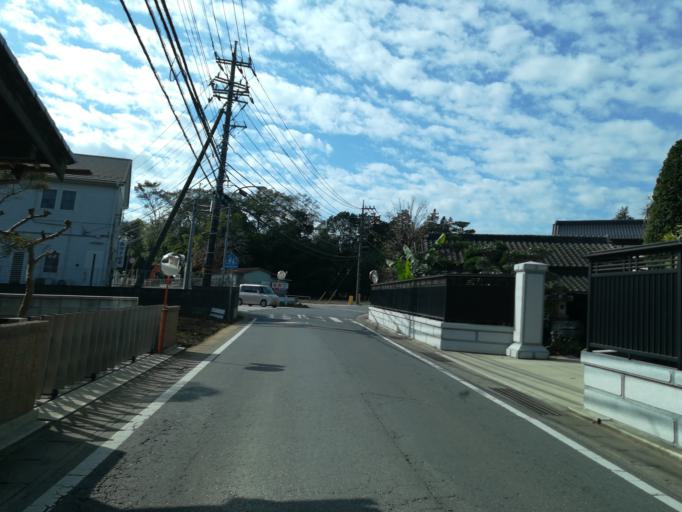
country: JP
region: Ibaraki
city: Naka
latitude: 36.0752
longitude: 140.0935
